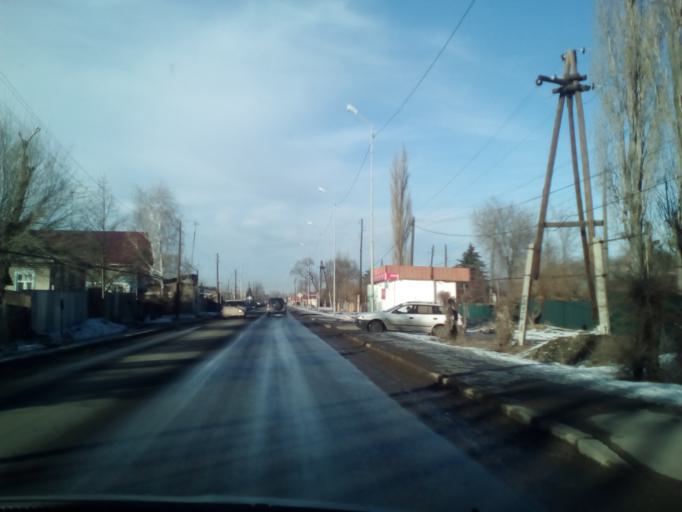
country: KZ
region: Almaty Oblysy
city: Burunday
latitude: 43.1693
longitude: 76.4163
